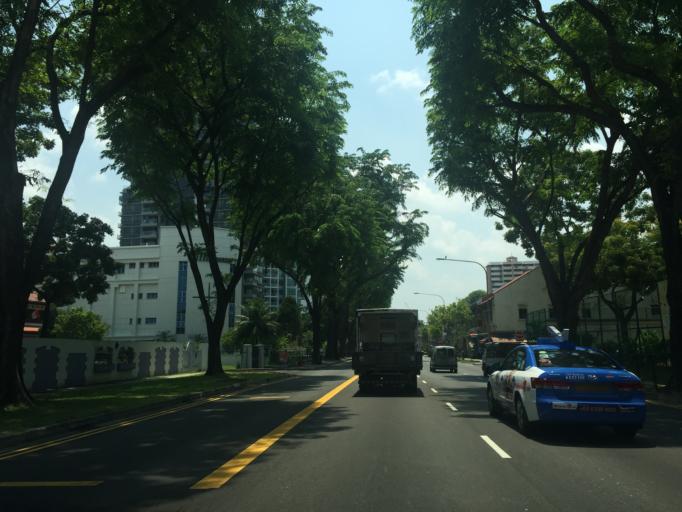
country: SG
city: Singapore
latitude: 1.3228
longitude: 103.8641
